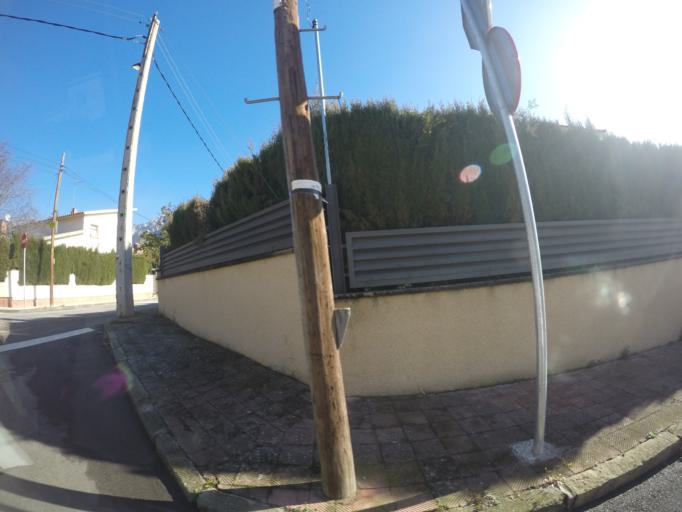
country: ES
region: Catalonia
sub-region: Provincia de Barcelona
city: Collbato
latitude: 41.5689
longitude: 1.8100
